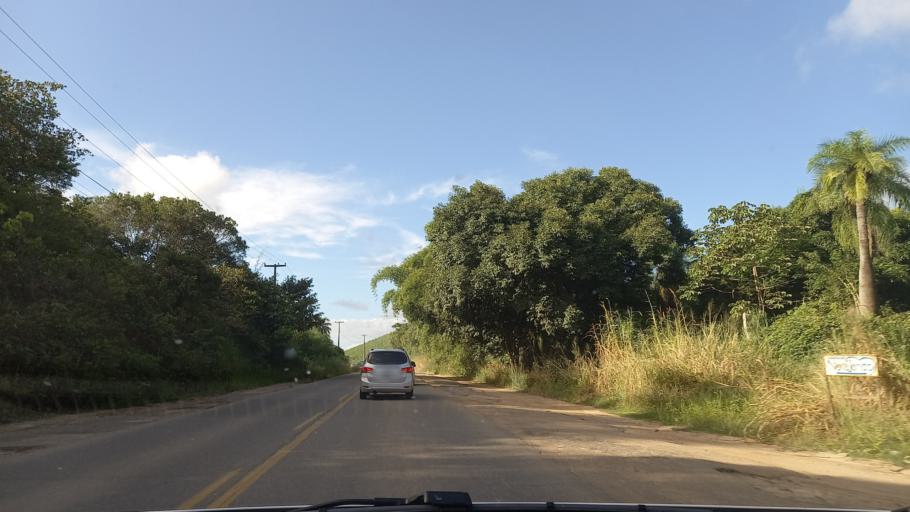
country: BR
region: Pernambuco
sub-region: Sirinhaem
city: Sirinhaem
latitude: -8.6149
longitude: -35.1201
